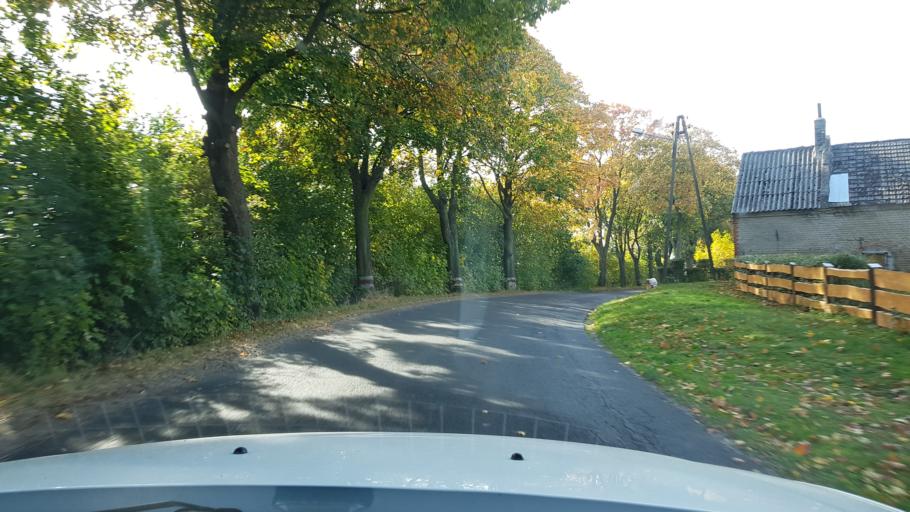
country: PL
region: West Pomeranian Voivodeship
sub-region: Powiat mysliborski
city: Nowogrodek Pomorski
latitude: 52.9433
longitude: 15.0945
